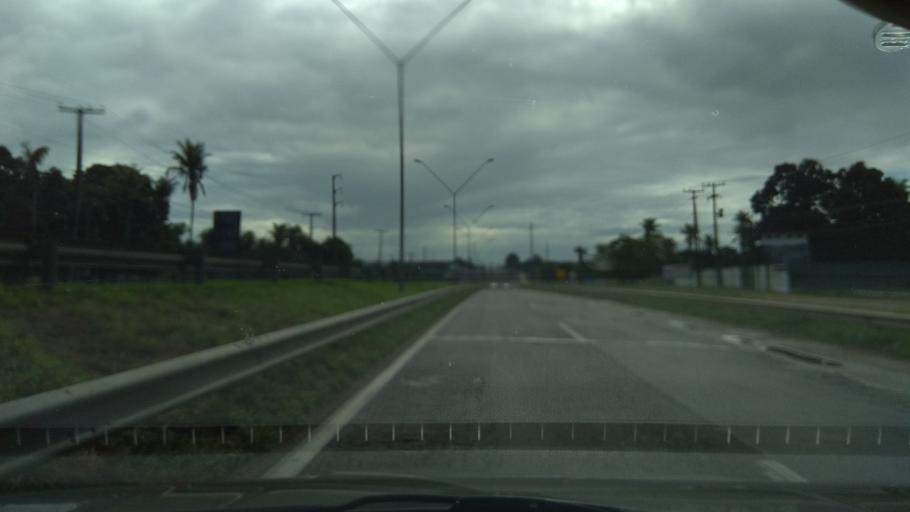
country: BR
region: Bahia
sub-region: Feira De Santana
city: Feira de Santana
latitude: -12.3031
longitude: -38.8948
